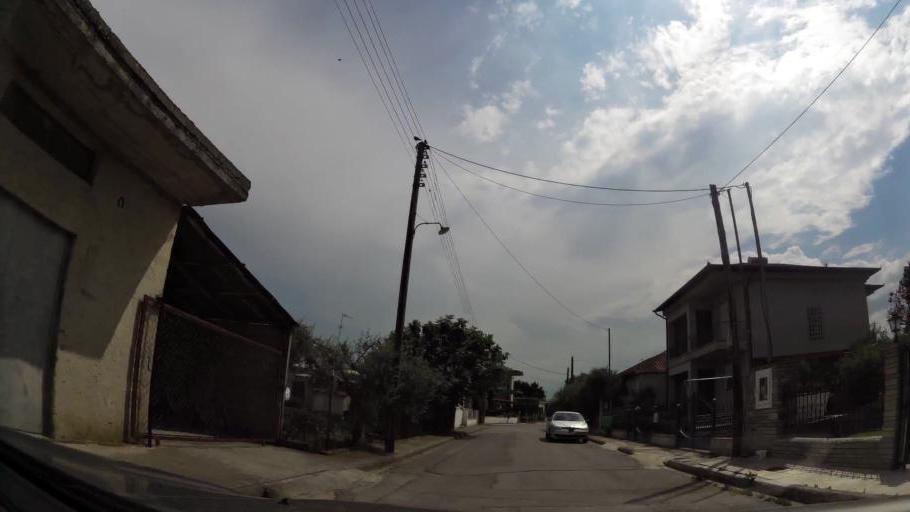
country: GR
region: Central Macedonia
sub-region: Nomos Pierias
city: Korinos
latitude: 40.3198
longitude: 22.5906
